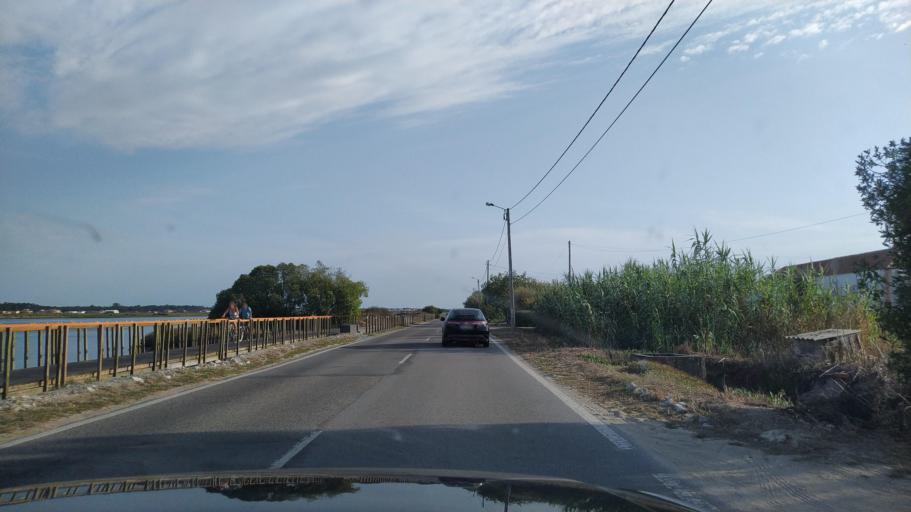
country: PT
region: Aveiro
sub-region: Ilhavo
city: Gafanha da Encarnacao
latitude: 40.5883
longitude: -8.7522
